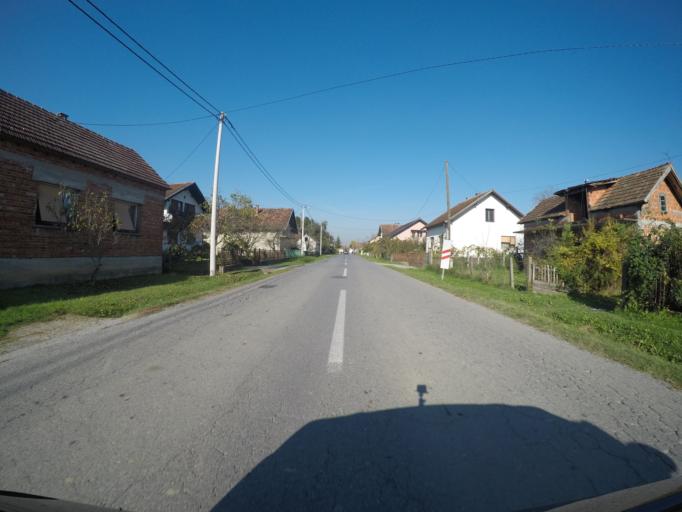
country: HR
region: Bjelovarsko-Bilogorska
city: Predavac
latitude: 45.9090
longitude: 16.7730
